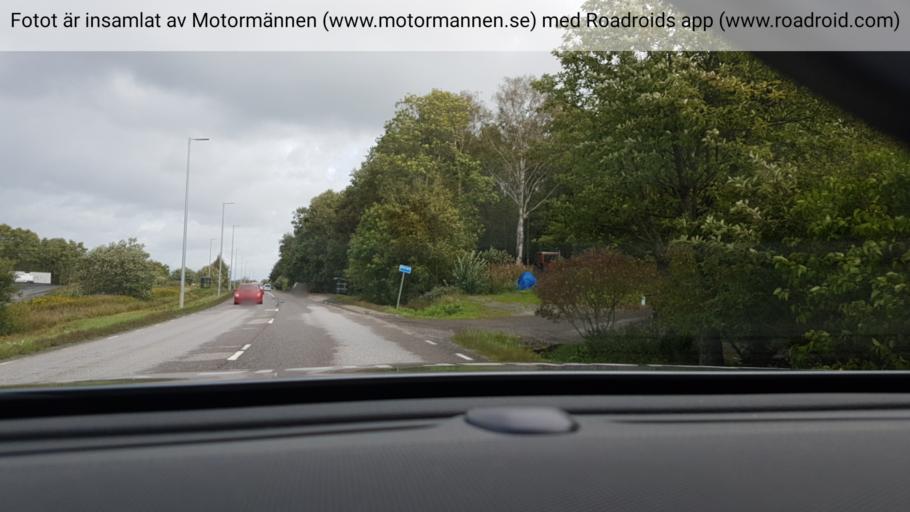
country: SE
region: Vaestra Goetaland
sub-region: Partille Kommun
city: Partille
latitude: 57.7930
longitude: 12.1321
